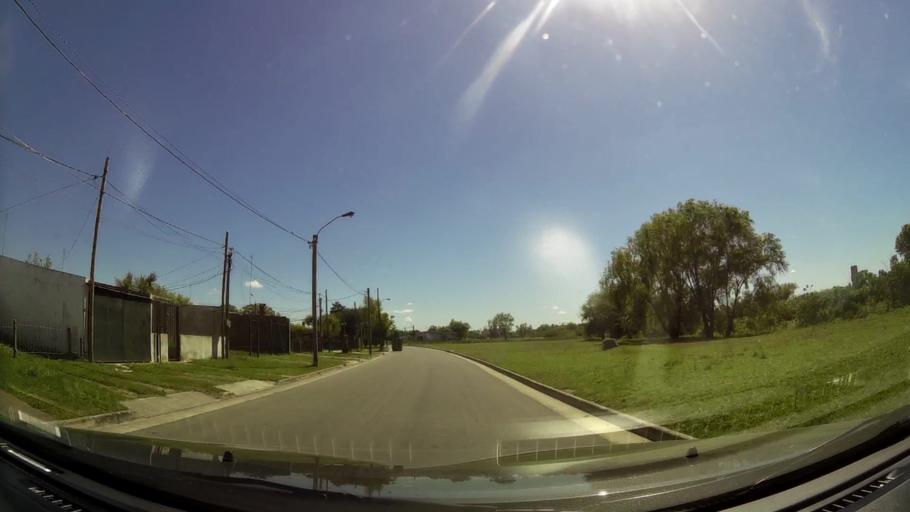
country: UY
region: Canelones
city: Paso de Carrasco
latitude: -34.8598
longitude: -56.1187
